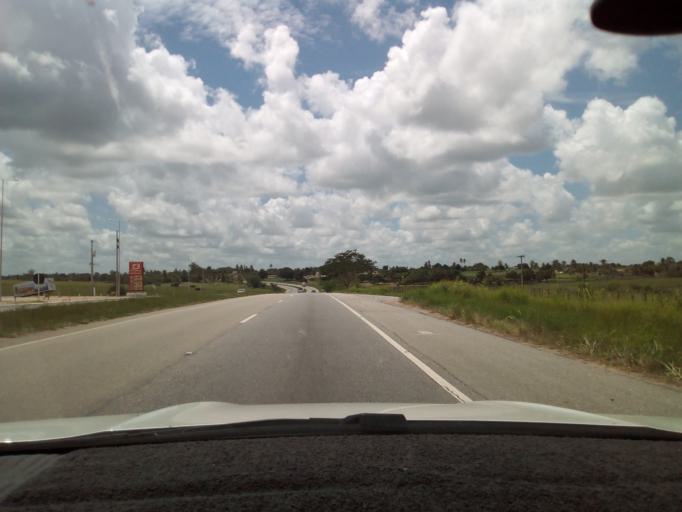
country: BR
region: Paraiba
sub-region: Pilar
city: Pilar
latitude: -7.1899
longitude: -35.2747
